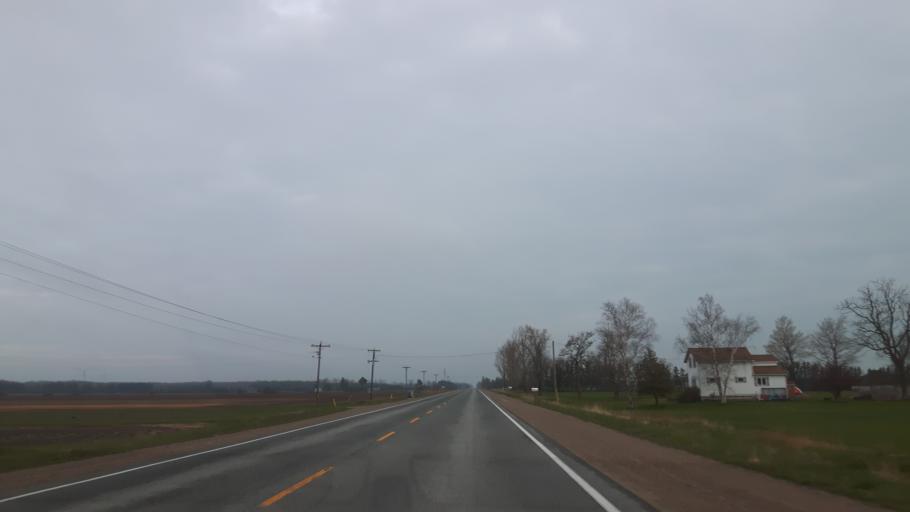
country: CA
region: Ontario
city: Bluewater
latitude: 43.5270
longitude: -81.6924
